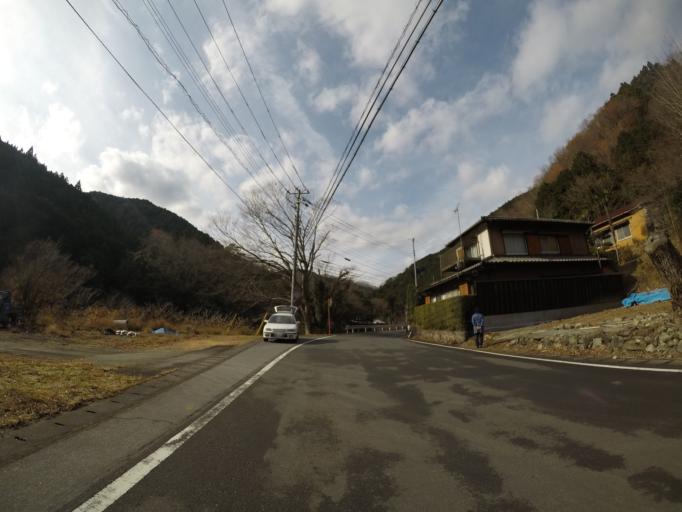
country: JP
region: Shizuoka
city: Heda
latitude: 34.8849
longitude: 138.9168
